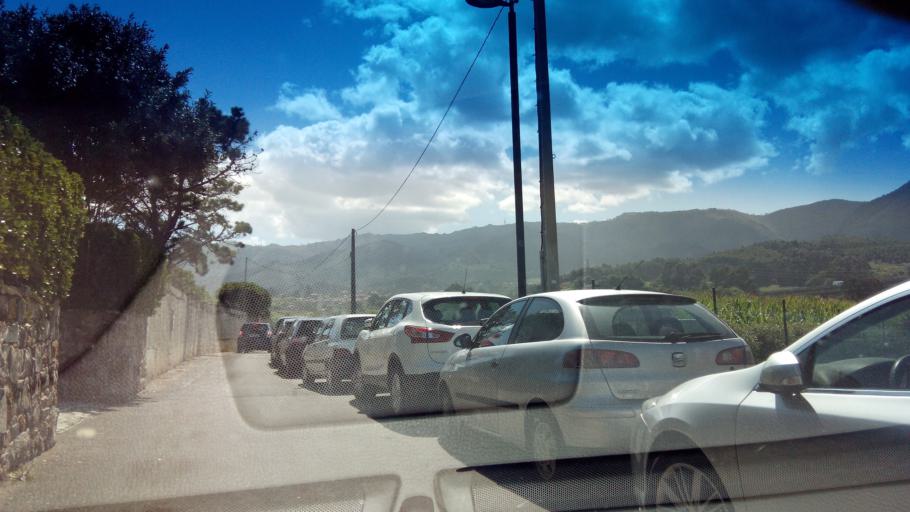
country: ES
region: Asturias
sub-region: Province of Asturias
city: Colunga
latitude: 43.4756
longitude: -5.2194
